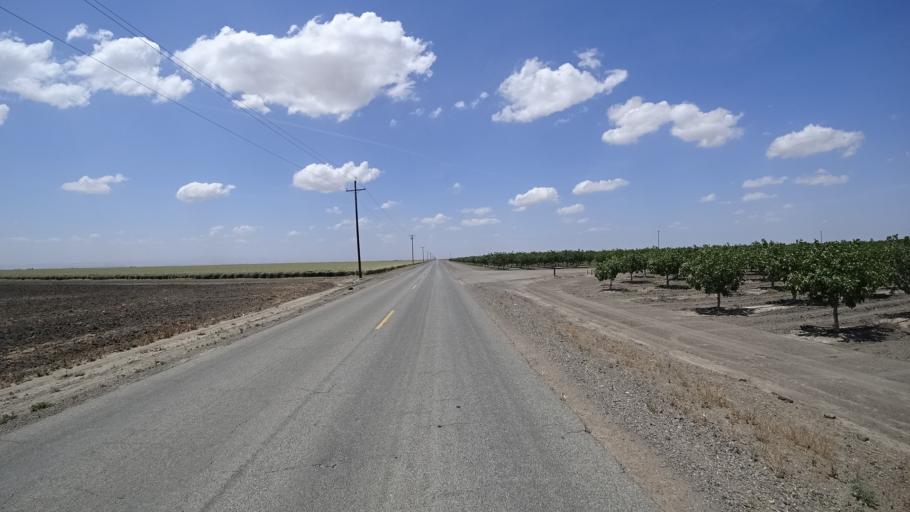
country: US
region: California
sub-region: Kings County
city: Stratford
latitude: 36.1895
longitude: -119.8552
